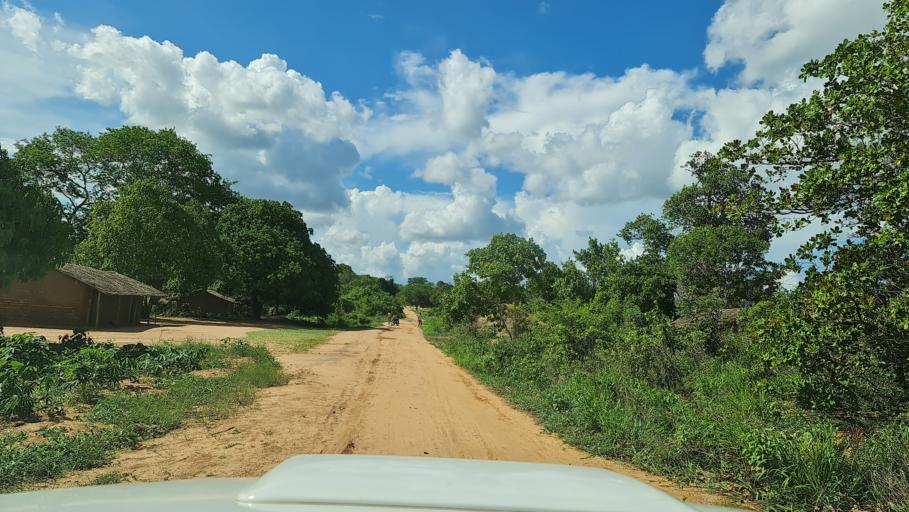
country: MZ
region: Nampula
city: Ilha de Mocambique
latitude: -15.4252
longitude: 40.2694
